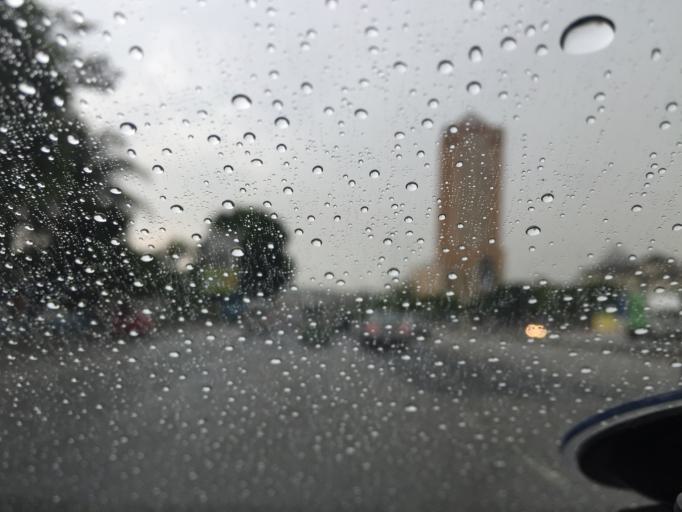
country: MY
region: Selangor
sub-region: Petaling
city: Petaling Jaya
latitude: 3.0733
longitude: 101.6012
